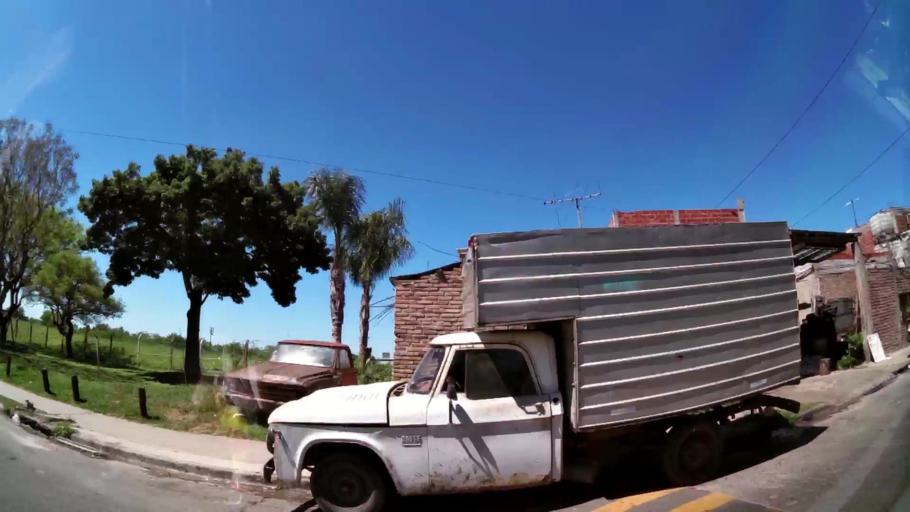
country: AR
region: Buenos Aires
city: Hurlingham
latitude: -34.5023
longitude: -58.6402
